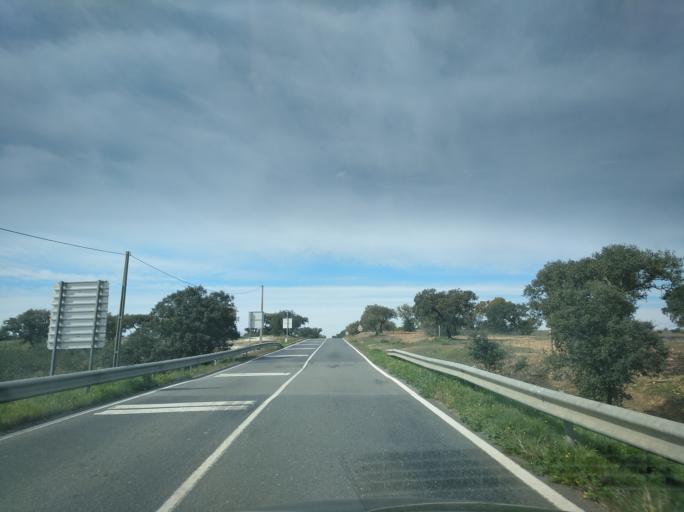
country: PT
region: Beja
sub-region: Mertola
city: Mertola
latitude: 37.7457
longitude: -7.7962
